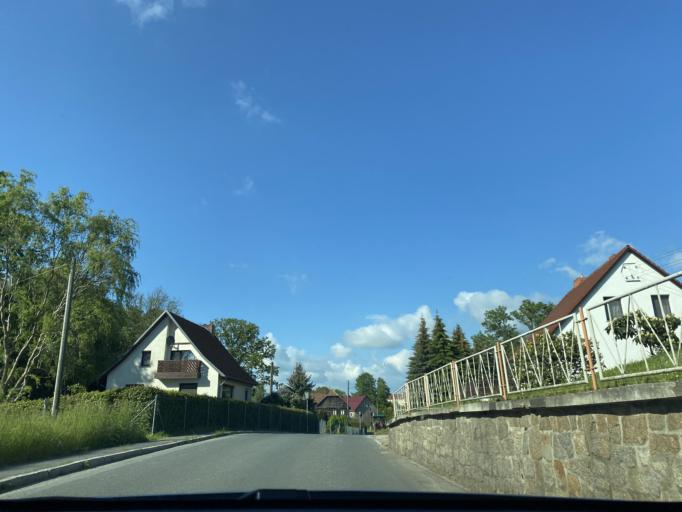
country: DE
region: Saxony
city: Markersdorf
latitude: 51.1341
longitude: 14.8788
